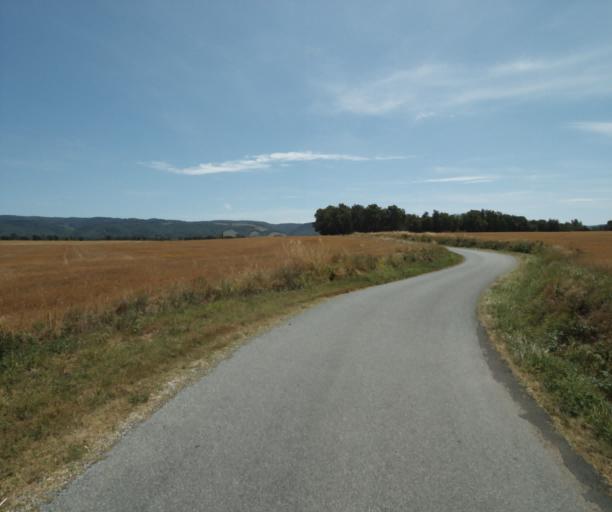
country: FR
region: Midi-Pyrenees
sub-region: Departement du Tarn
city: Soreze
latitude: 43.4871
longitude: 2.0568
